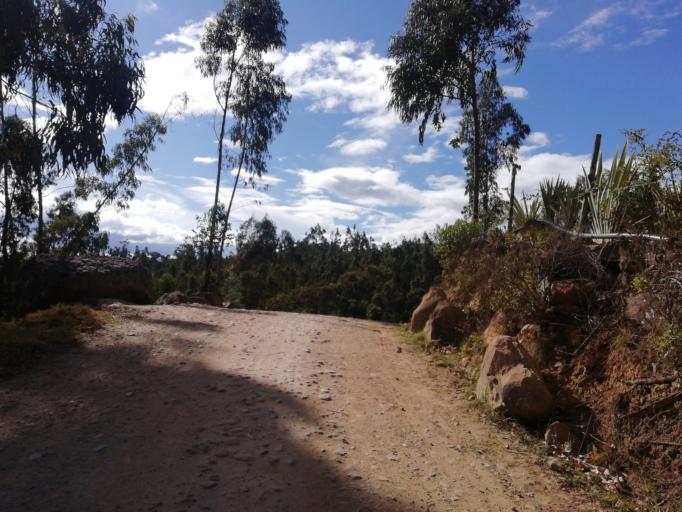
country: CO
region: Boyaca
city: Gameza
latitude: 5.8079
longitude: -72.8099
